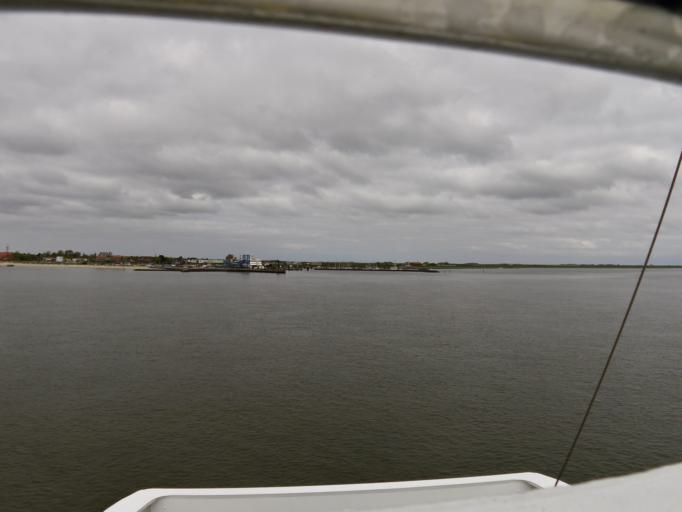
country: DE
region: Schleswig-Holstein
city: Wyk auf Fohr
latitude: 54.6900
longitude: 8.5838
